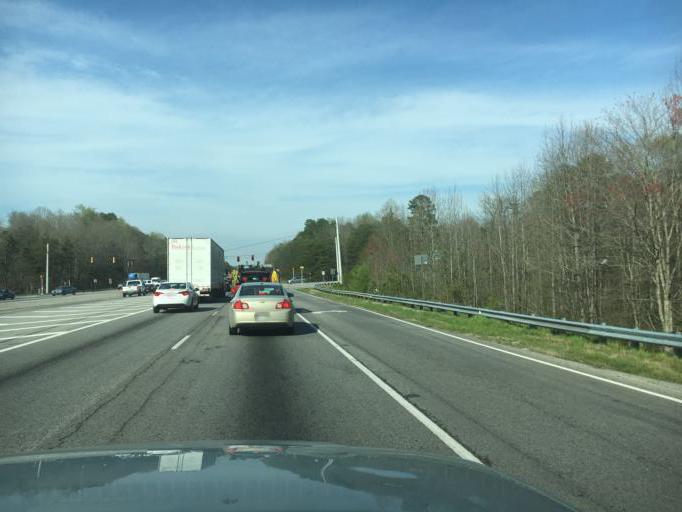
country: US
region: Georgia
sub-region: Banks County
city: Alto
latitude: 34.4965
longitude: -83.5757
